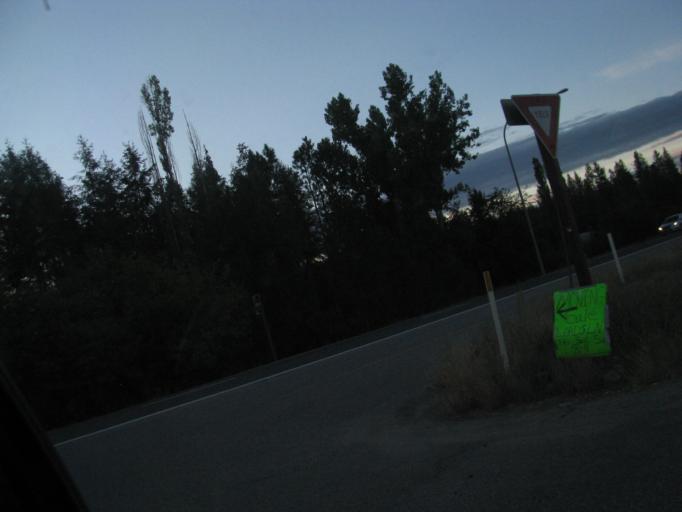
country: US
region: Washington
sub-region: Spokane County
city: Mead
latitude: 47.8894
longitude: -117.3539
